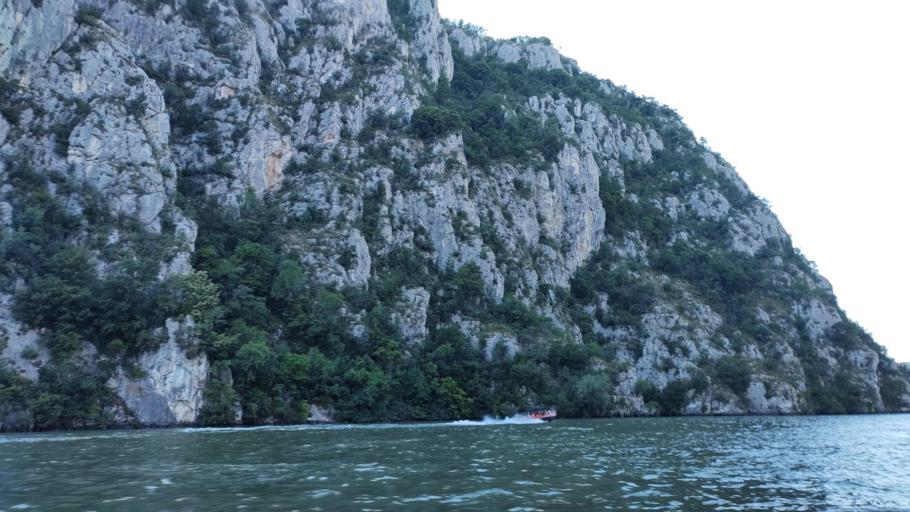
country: RO
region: Mehedinti
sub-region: Comuna Dubova
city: Dubova
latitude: 44.6121
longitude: 22.2715
